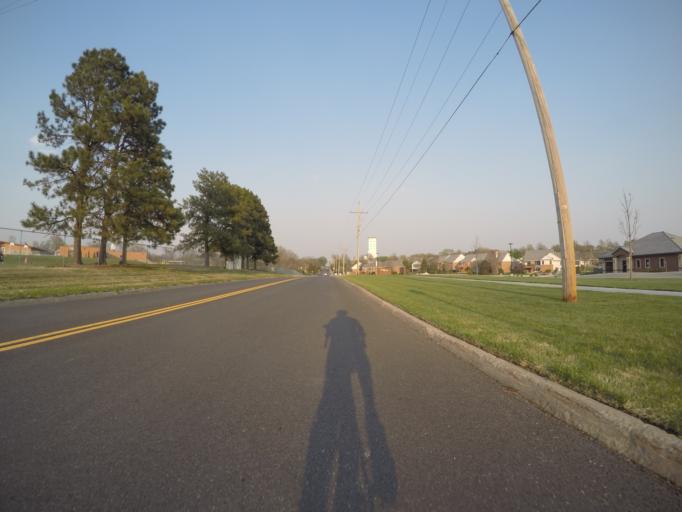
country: US
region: Kansas
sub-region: Riley County
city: Manhattan
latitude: 39.1964
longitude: -96.6073
